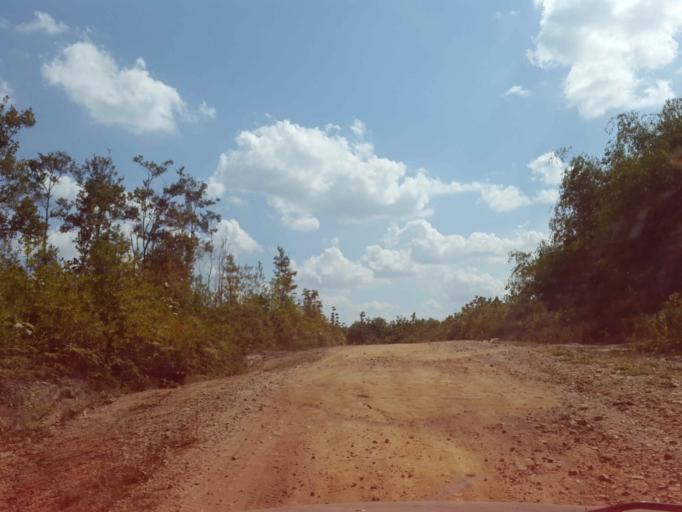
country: MY
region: Sarawak
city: Simanggang
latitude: 0.7270
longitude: 111.5637
